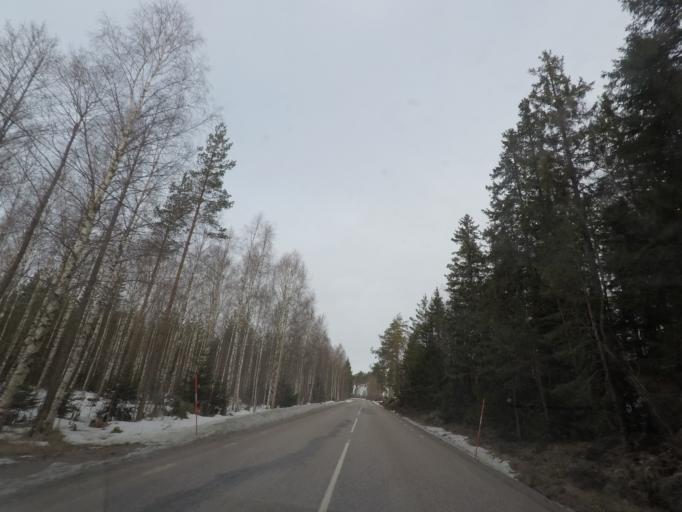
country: SE
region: Vaestmanland
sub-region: Vasteras
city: Skultuna
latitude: 59.7505
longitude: 16.3244
